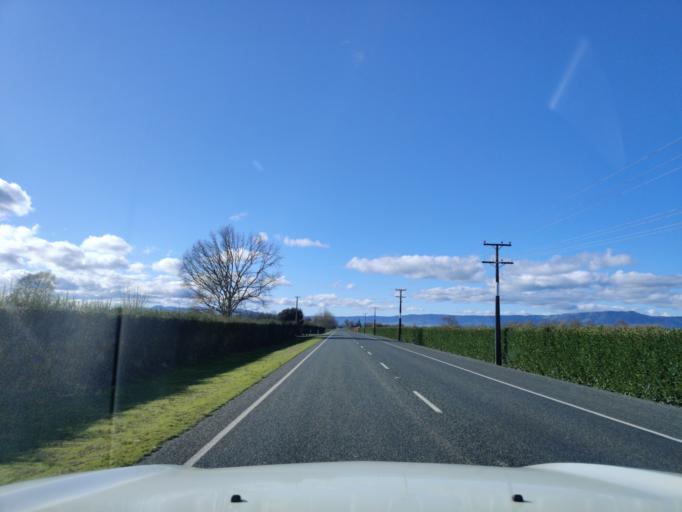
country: NZ
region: Waikato
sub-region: Matamata-Piako District
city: Matamata
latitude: -37.8743
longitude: 175.7424
